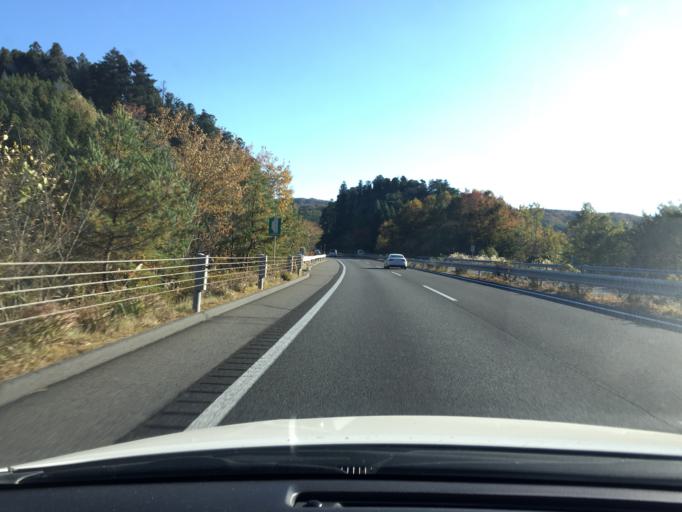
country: JP
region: Fukushima
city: Ishikawa
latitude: 37.2134
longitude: 140.6913
